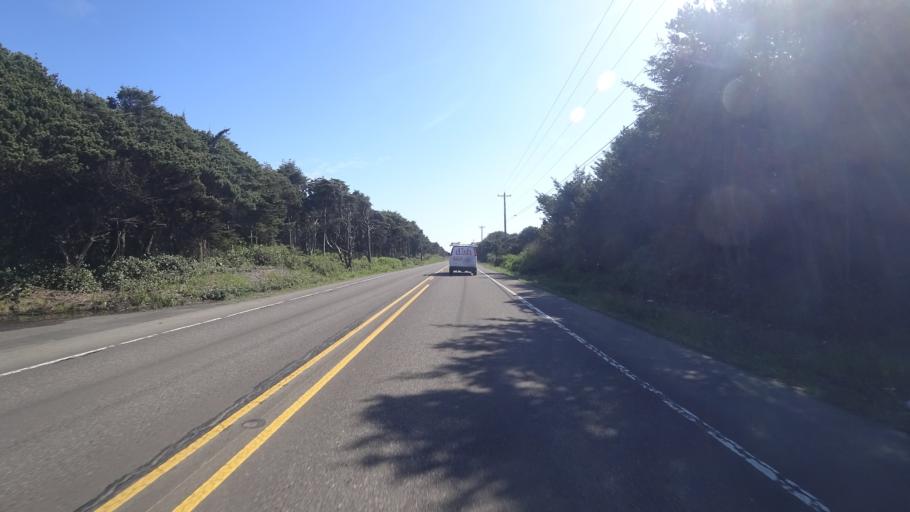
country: US
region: Oregon
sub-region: Lincoln County
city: Newport
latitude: 44.5602
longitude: -124.0705
